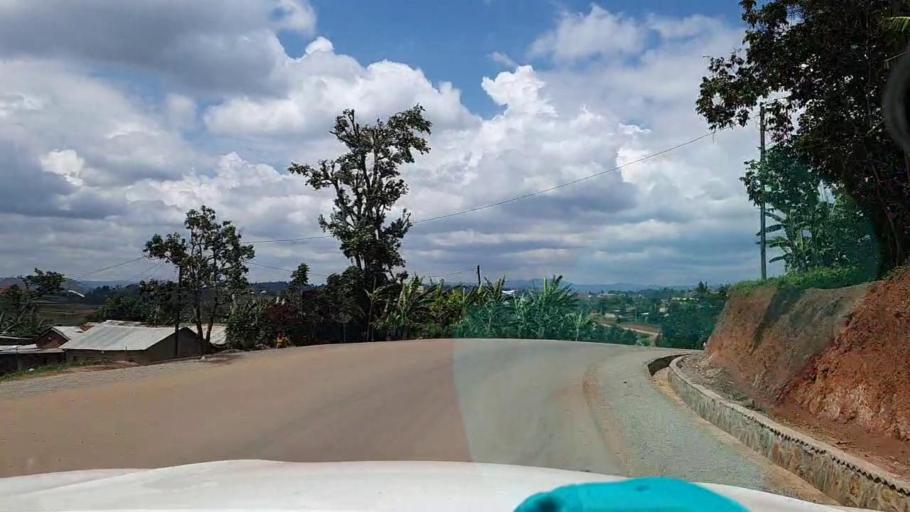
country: RW
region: Southern Province
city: Nzega
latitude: -2.6472
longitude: 29.5681
